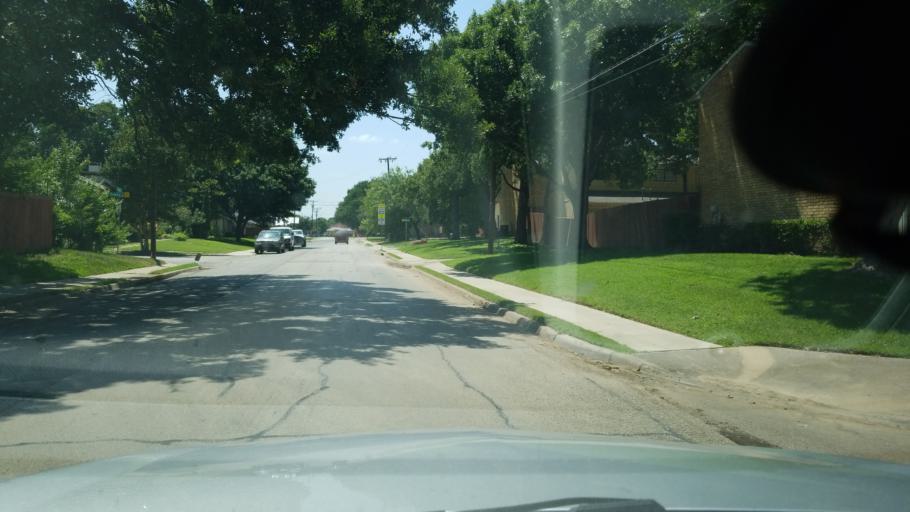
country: US
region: Texas
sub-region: Dallas County
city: Irving
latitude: 32.8124
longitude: -96.9563
